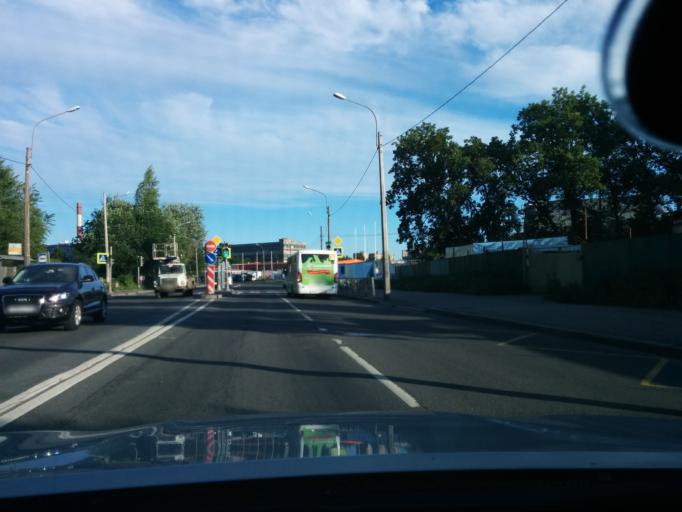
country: RU
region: Leningrad
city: Finlyandskiy
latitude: 59.9783
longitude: 30.3671
